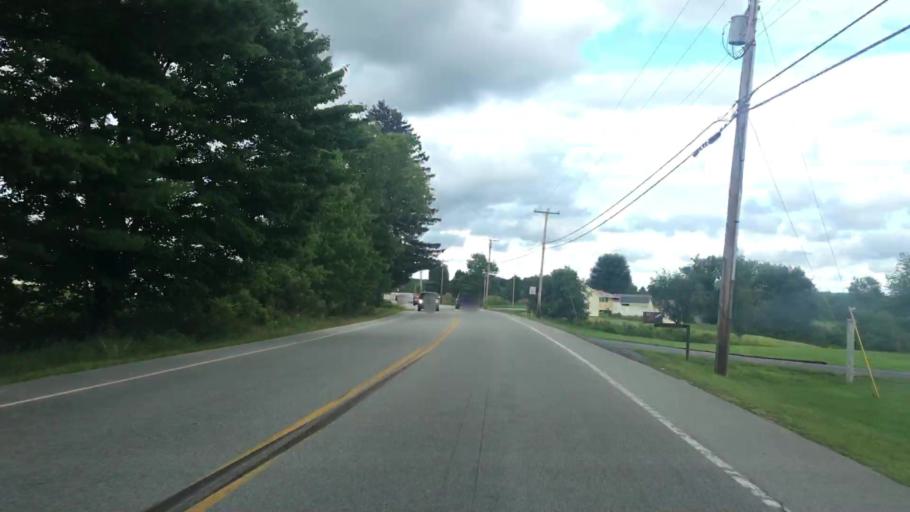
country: US
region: Maine
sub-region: York County
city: Dayton
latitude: 43.5411
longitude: -70.5744
